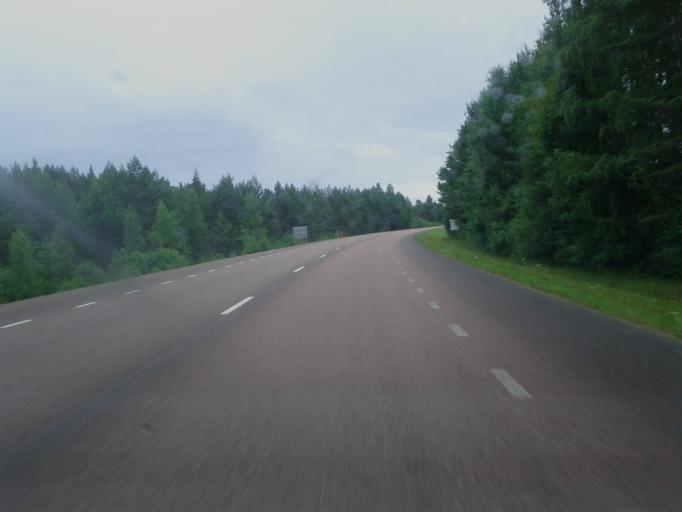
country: SE
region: Dalarna
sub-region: Mora Kommun
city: Mora
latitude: 61.0203
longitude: 14.5379
